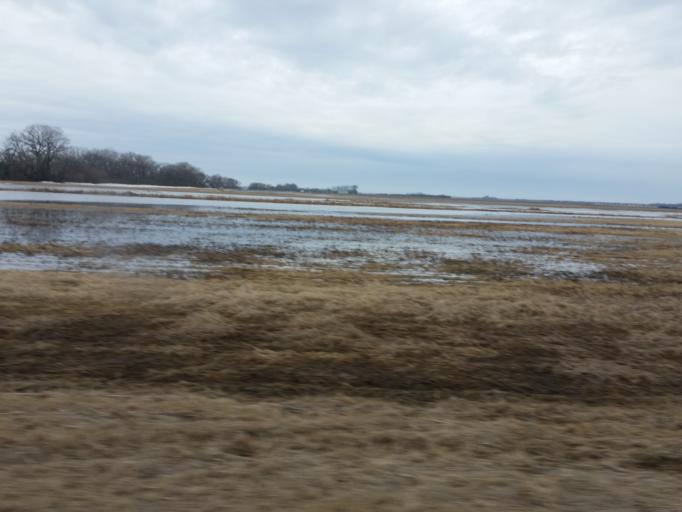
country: US
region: North Dakota
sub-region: Walsh County
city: Grafton
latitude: 48.4064
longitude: -97.4702
